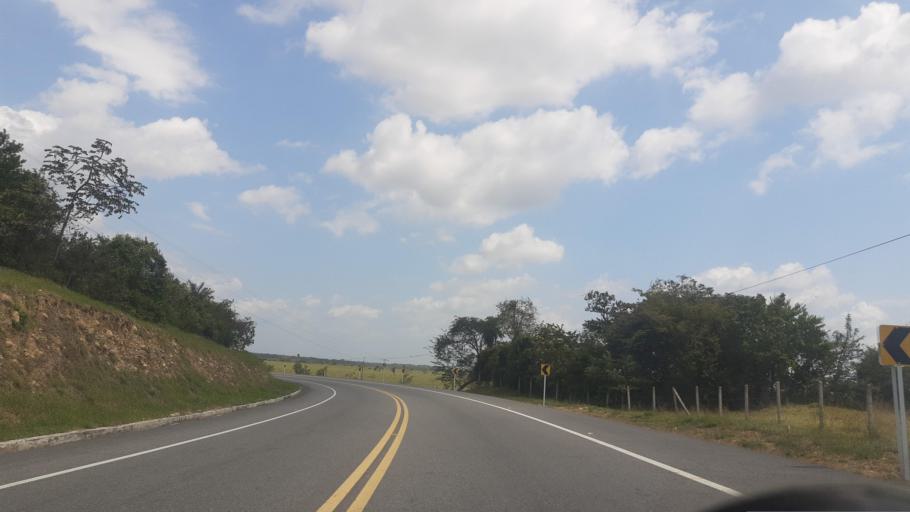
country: CO
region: Casanare
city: Tauramena
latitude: 4.8973
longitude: -72.6775
